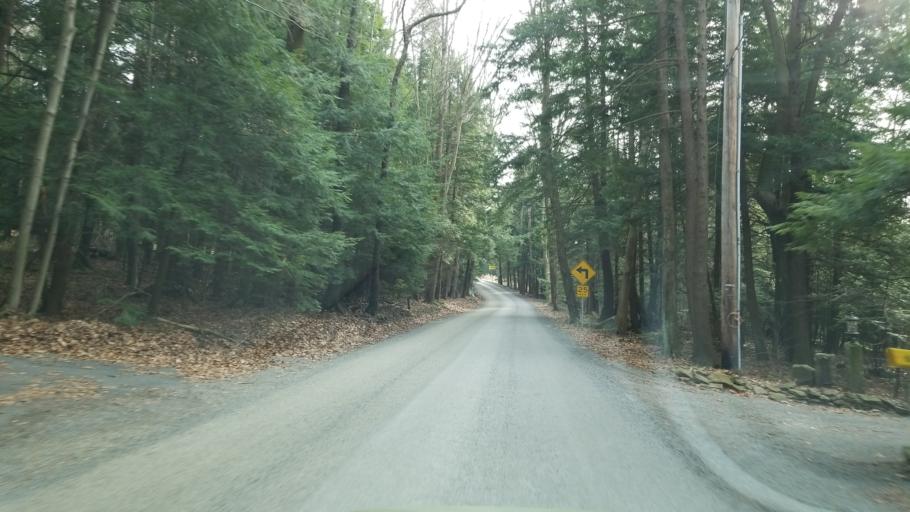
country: US
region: Pennsylvania
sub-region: Indiana County
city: Johnsonburg
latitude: 40.9405
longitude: -78.8922
